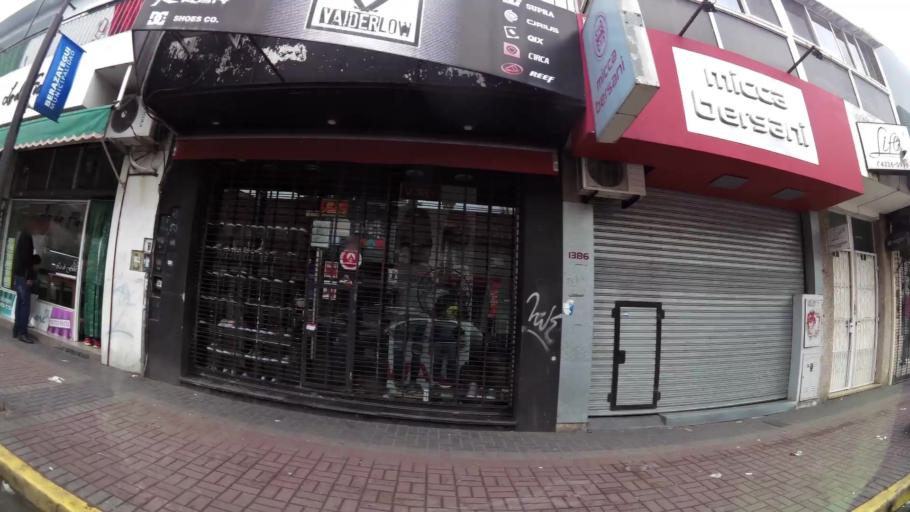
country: AR
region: Buenos Aires
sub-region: Partido de Quilmes
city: Quilmes
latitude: -34.7616
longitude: -58.2095
